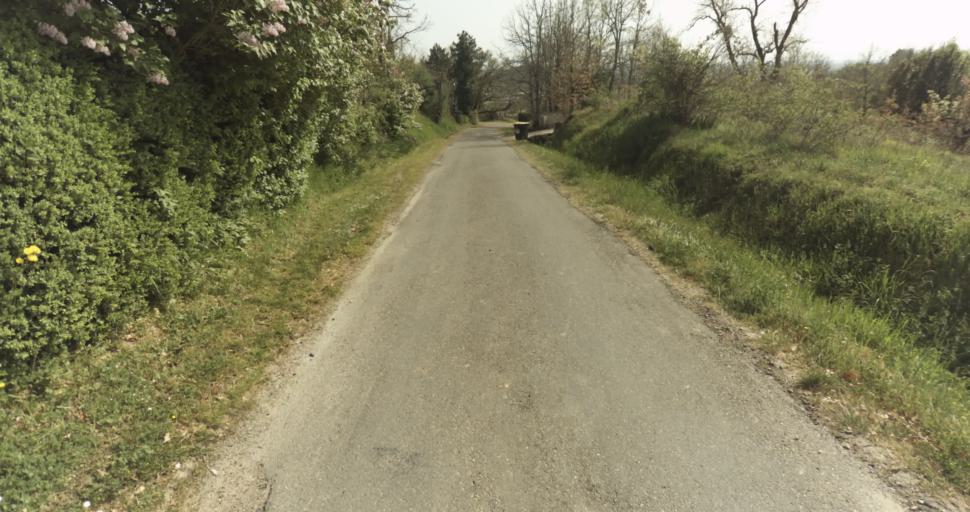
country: FR
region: Midi-Pyrenees
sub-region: Departement du Tarn-et-Garonne
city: Moissac
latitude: 44.1315
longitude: 1.1488
